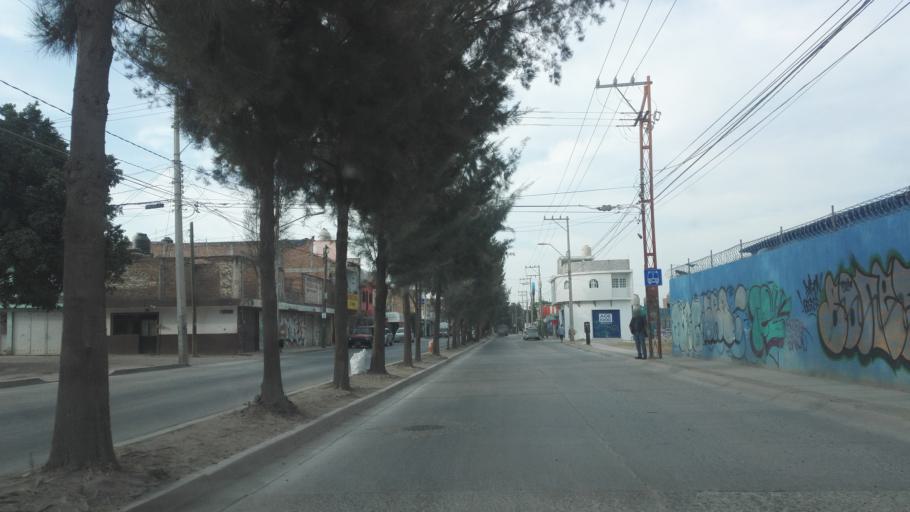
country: MX
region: Guanajuato
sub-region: Leon
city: Fraccionamiento Paraiso Real
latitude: 21.0989
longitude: -101.6026
